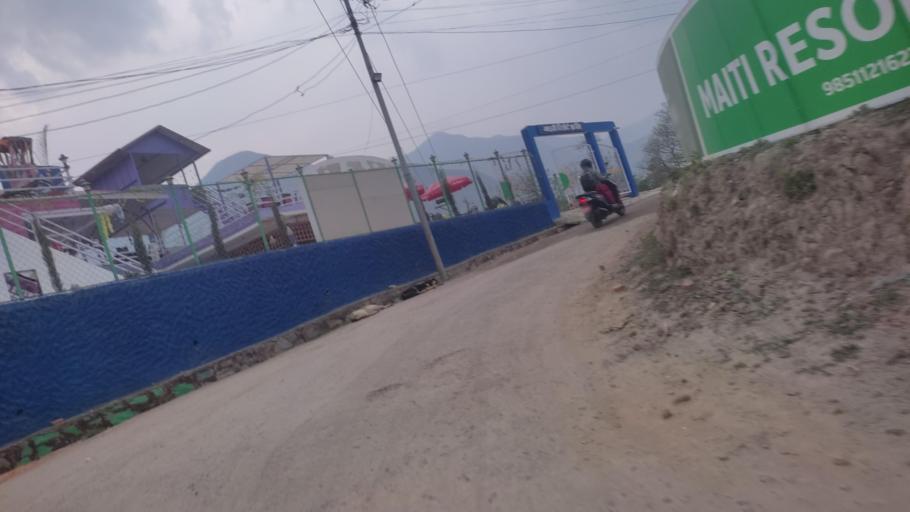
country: NP
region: Central Region
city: Kirtipur
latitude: 27.6606
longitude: 85.2822
